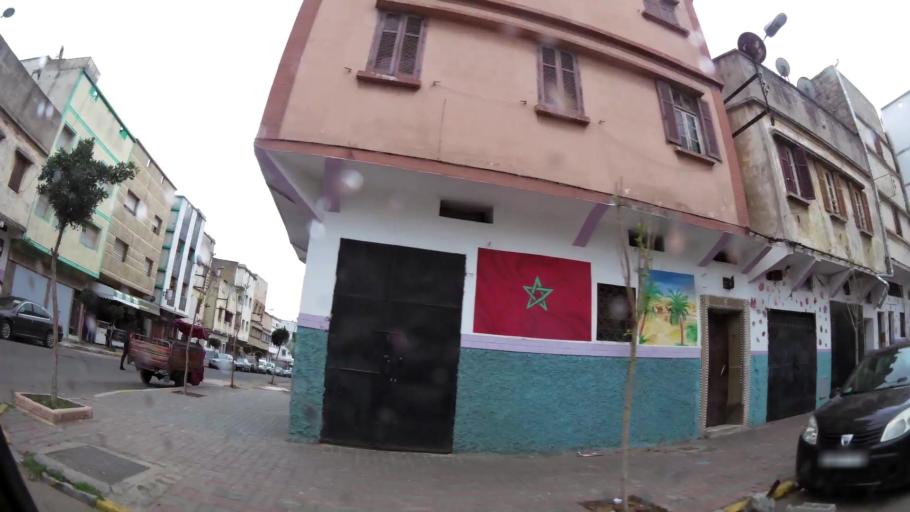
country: MA
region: Grand Casablanca
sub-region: Casablanca
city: Casablanca
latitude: 33.5621
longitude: -7.5648
